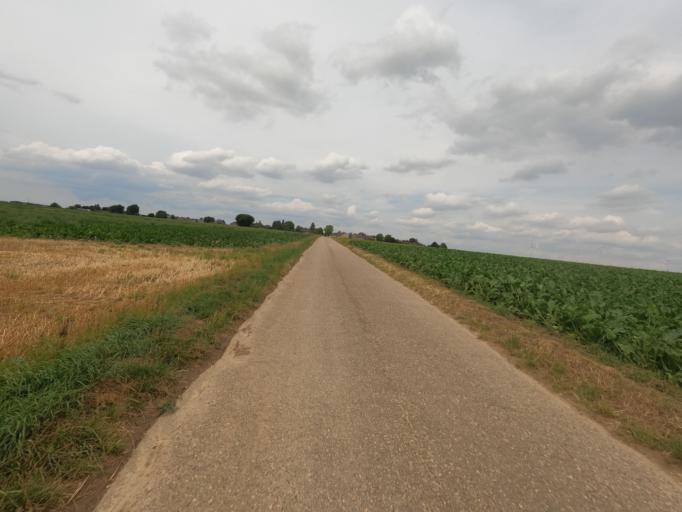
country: DE
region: North Rhine-Westphalia
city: Siersdorf
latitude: 50.9217
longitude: 6.2532
